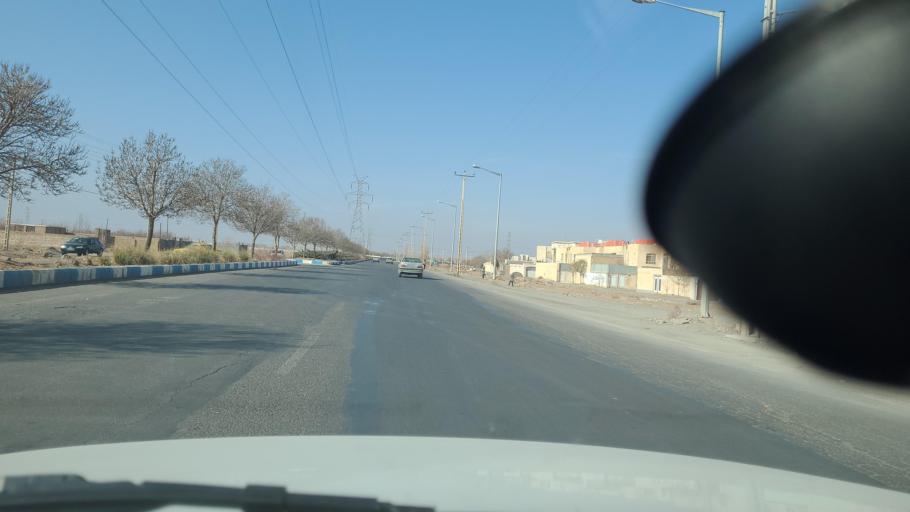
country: IR
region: Razavi Khorasan
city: Fariman
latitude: 35.6970
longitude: 59.8405
